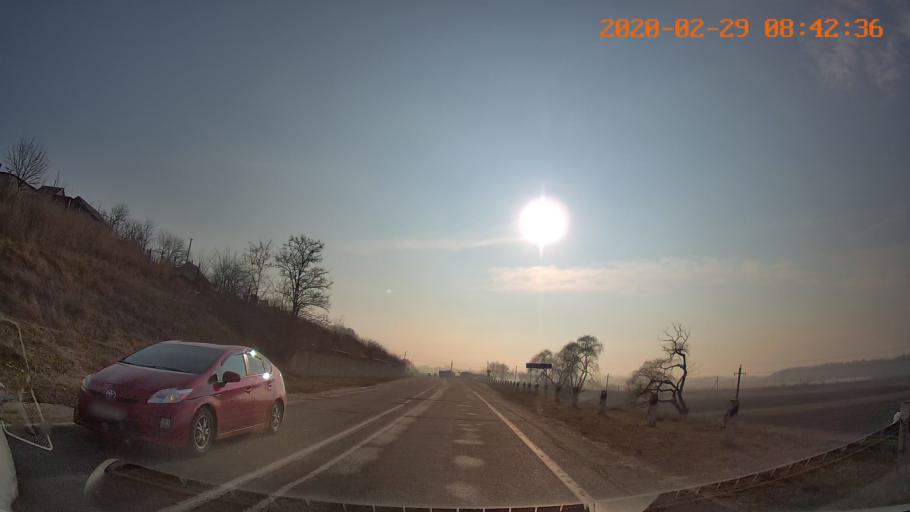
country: MD
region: Anenii Noi
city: Varnita
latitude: 46.9216
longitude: 29.4525
